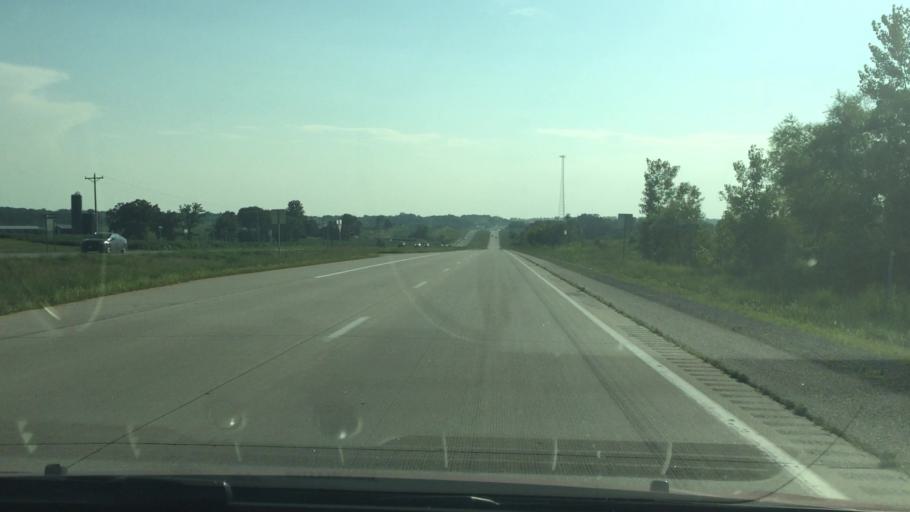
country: US
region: Iowa
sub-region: Cedar County
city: Durant
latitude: 41.5117
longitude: -90.9166
